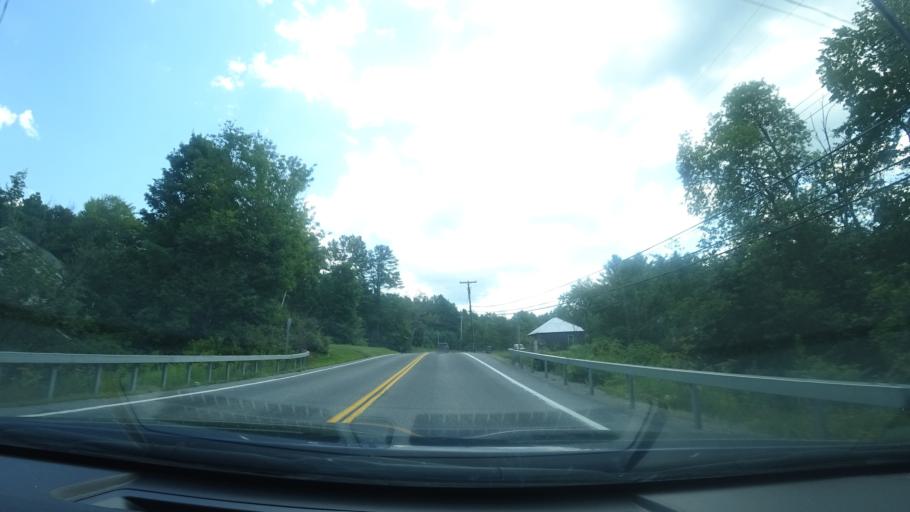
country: US
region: New York
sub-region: Warren County
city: Warrensburg
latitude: 43.6607
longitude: -73.8186
